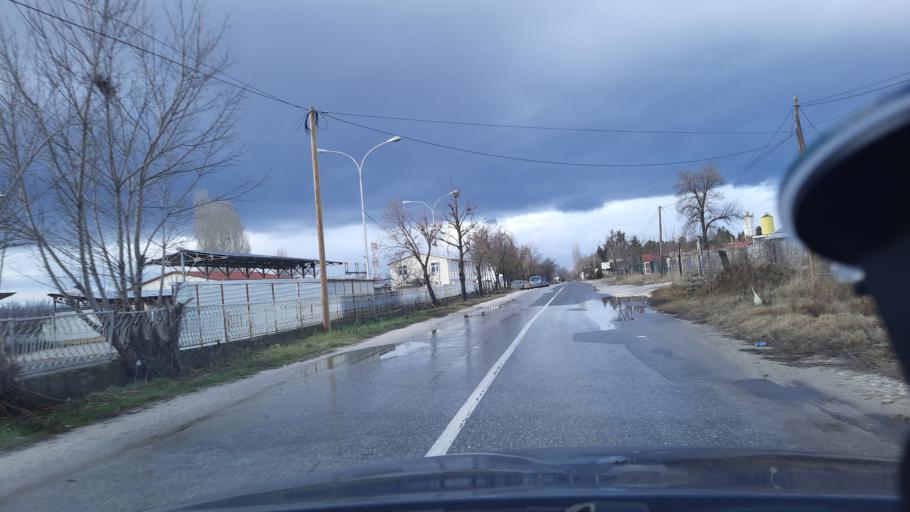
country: MK
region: Prilep
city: Markov Grad
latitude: 41.3431
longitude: 21.5254
